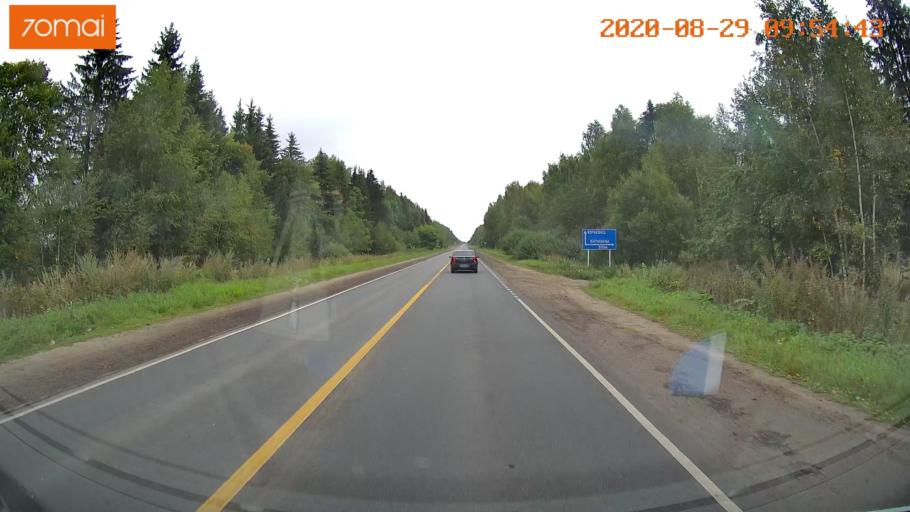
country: RU
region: Ivanovo
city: Zarechnyy
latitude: 57.4234
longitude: 42.2452
